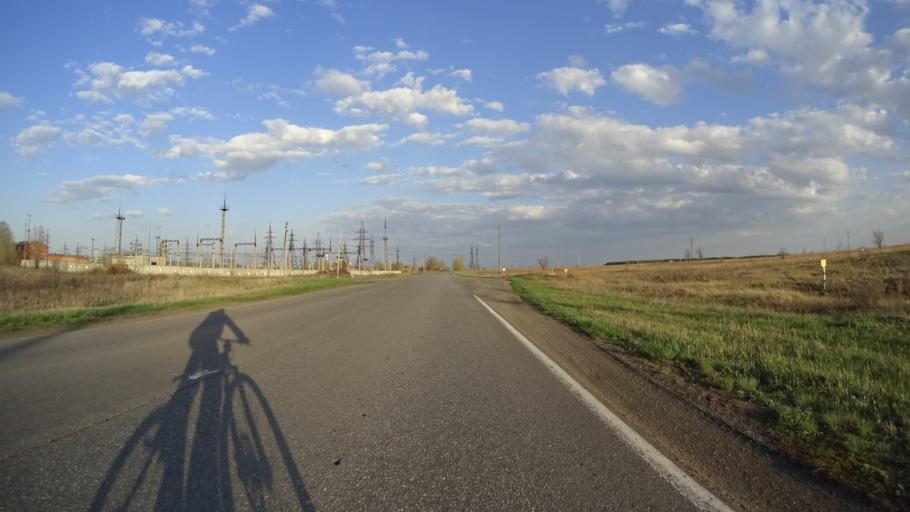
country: RU
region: Chelyabinsk
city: Troitsk
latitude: 54.0590
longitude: 61.5806
